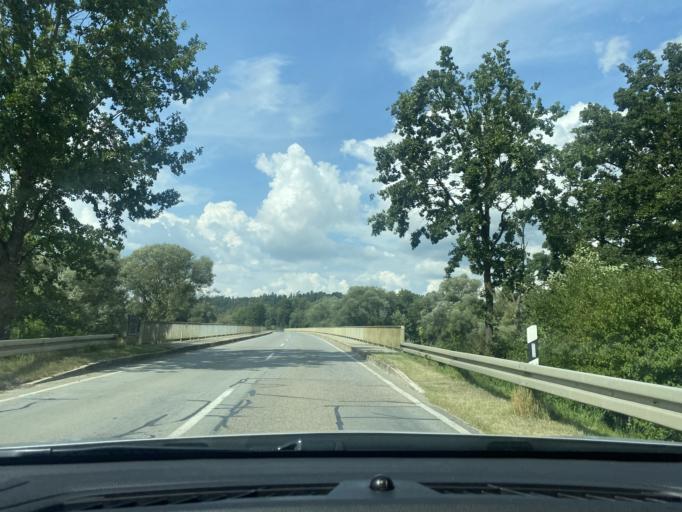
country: DE
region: Bavaria
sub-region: Upper Bavaria
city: Langenbach
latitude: 48.4556
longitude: 11.8526
